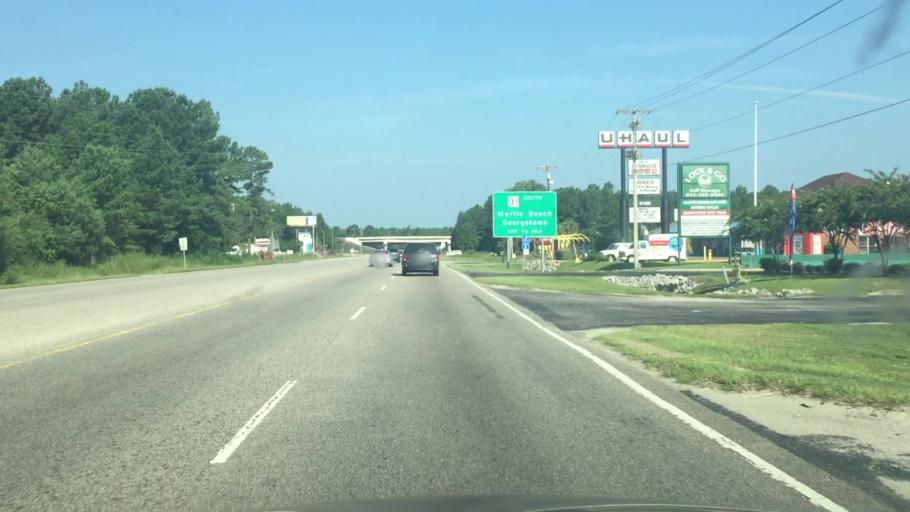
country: US
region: South Carolina
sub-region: Horry County
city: North Myrtle Beach
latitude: 33.8735
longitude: -78.6767
